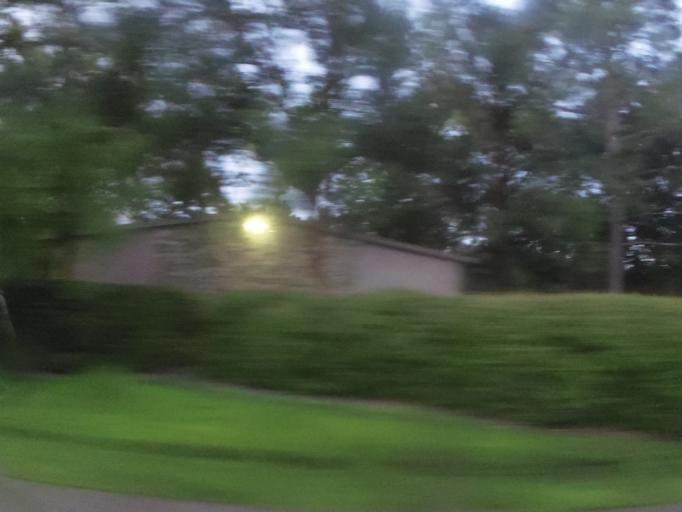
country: US
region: Florida
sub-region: Duval County
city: Jacksonville
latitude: 30.2463
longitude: -81.6172
